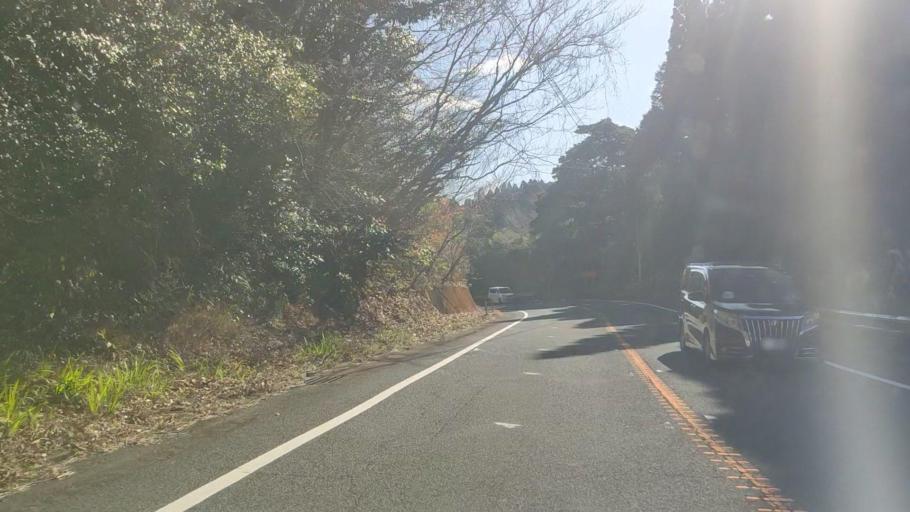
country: JP
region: Kagoshima
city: Sueyoshicho-ninokata
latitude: 31.6624
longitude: 130.8859
